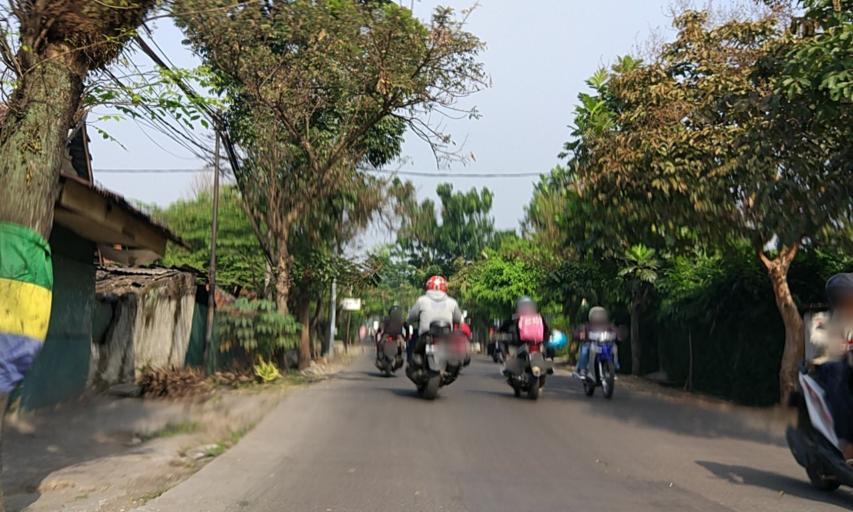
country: ID
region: West Java
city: Bandung
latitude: -6.9014
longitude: 107.6362
